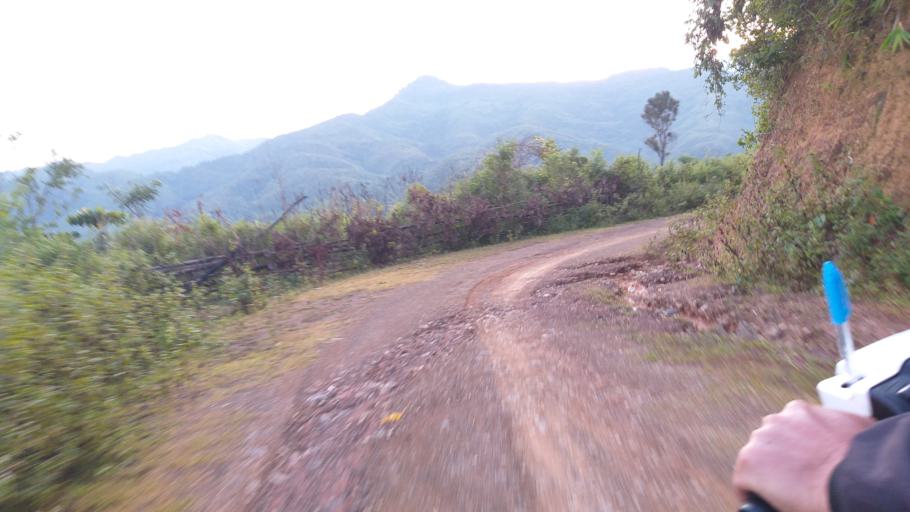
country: LA
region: Phongsali
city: Khoa
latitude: 21.4023
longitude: 102.6339
